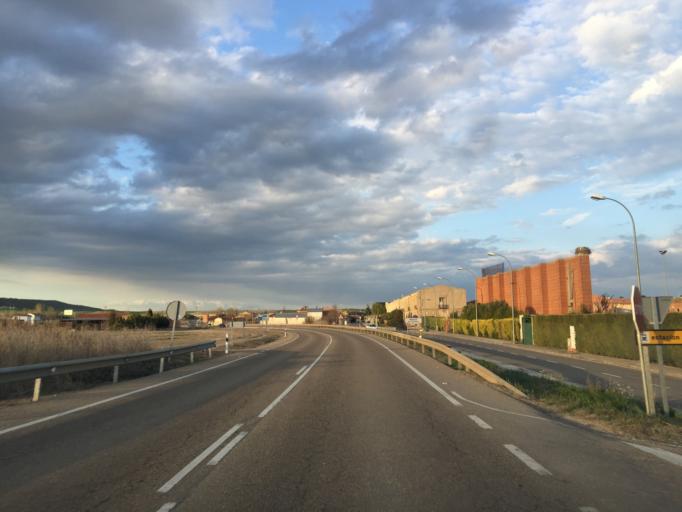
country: ES
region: Castille and Leon
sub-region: Provincia de Palencia
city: Soto de Cerrato
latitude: 41.9789
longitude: -4.4328
